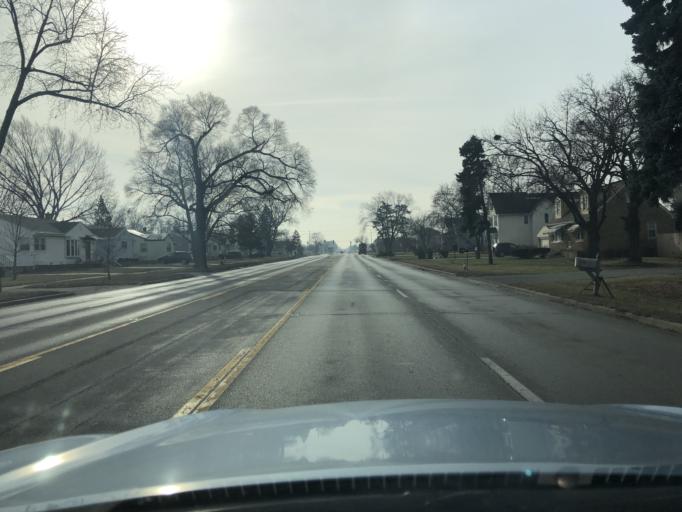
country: US
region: Illinois
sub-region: Cook County
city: Des Plaines
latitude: 42.0262
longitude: -87.9091
